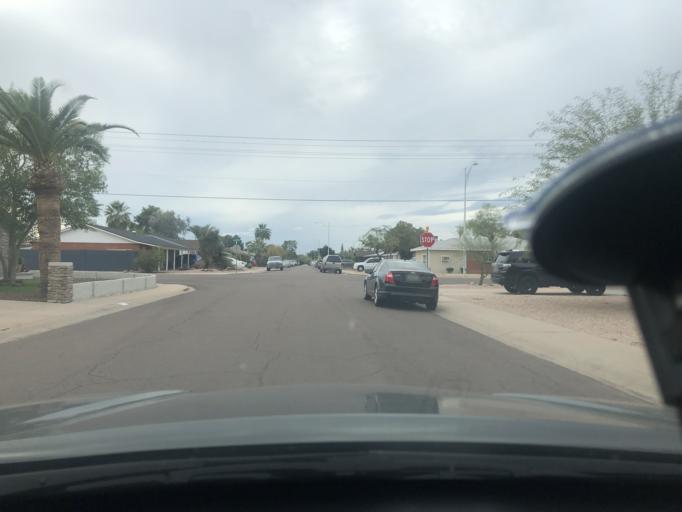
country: US
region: Arizona
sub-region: Maricopa County
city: Scottsdale
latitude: 33.4898
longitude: -111.9042
